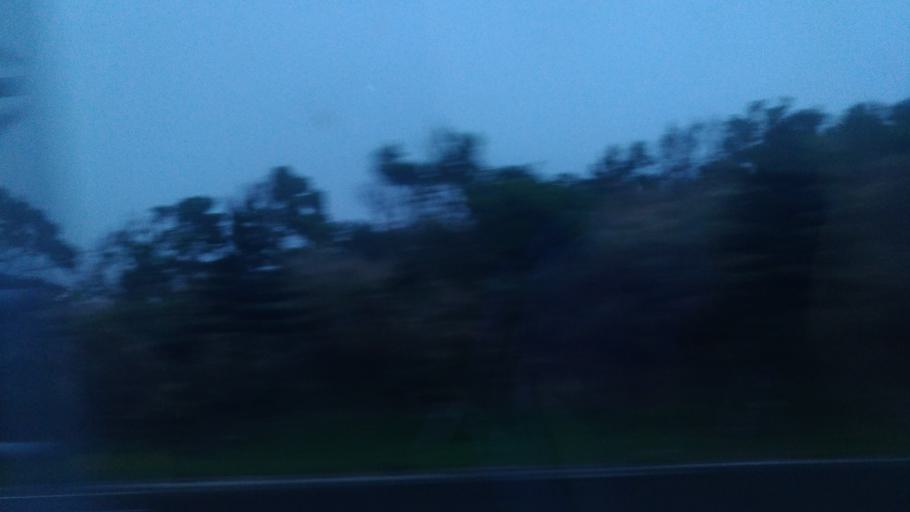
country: TW
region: Taiwan
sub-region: Miaoli
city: Miaoli
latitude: 24.5955
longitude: 120.7387
